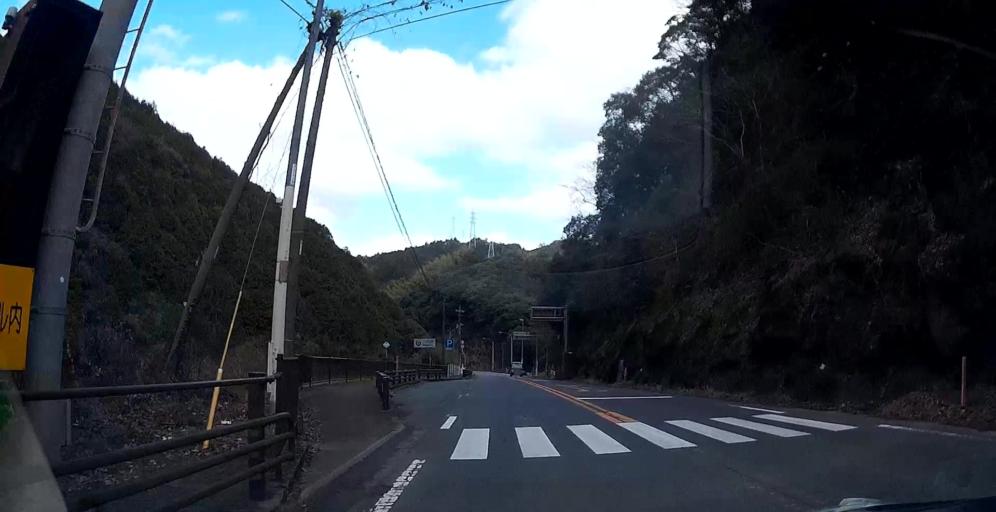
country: JP
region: Kumamoto
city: Yatsushiro
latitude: 32.3741
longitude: 130.5351
